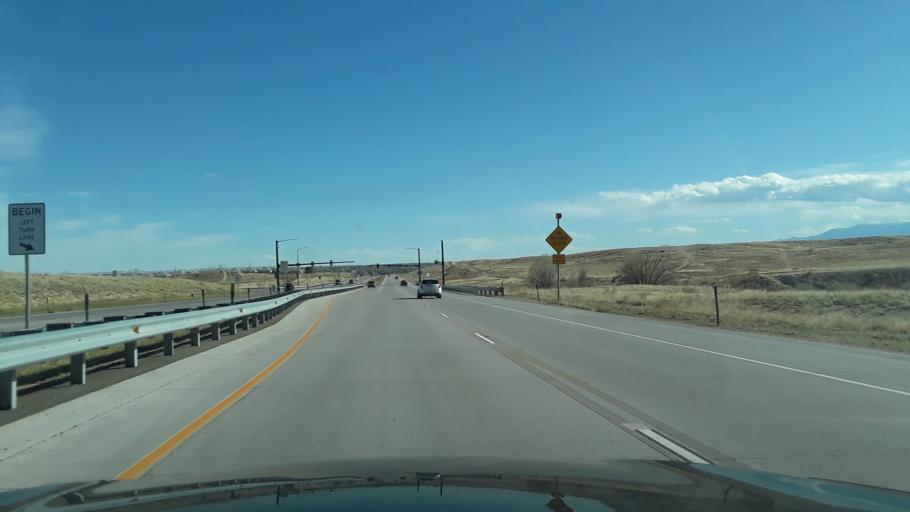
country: US
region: Colorado
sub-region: Pueblo County
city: Pueblo
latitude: 38.2942
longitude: -104.6635
